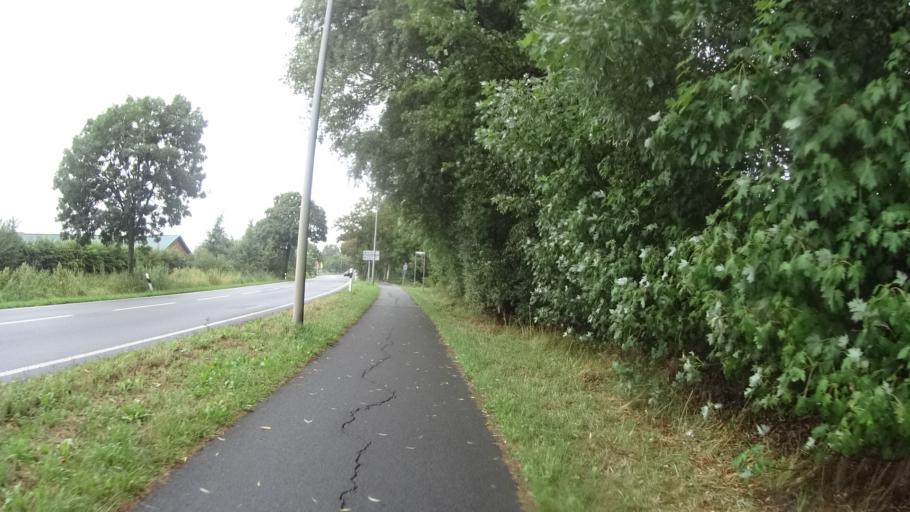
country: DE
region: Lower Saxony
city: Leer
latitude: 53.2190
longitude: 7.4363
